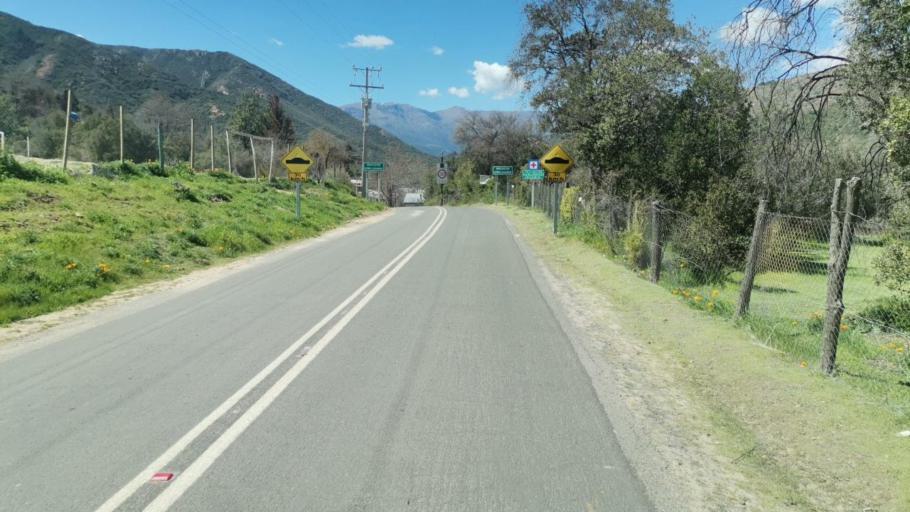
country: CL
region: Valparaiso
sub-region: Provincia de Marga Marga
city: Limache
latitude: -33.1687
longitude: -71.1456
